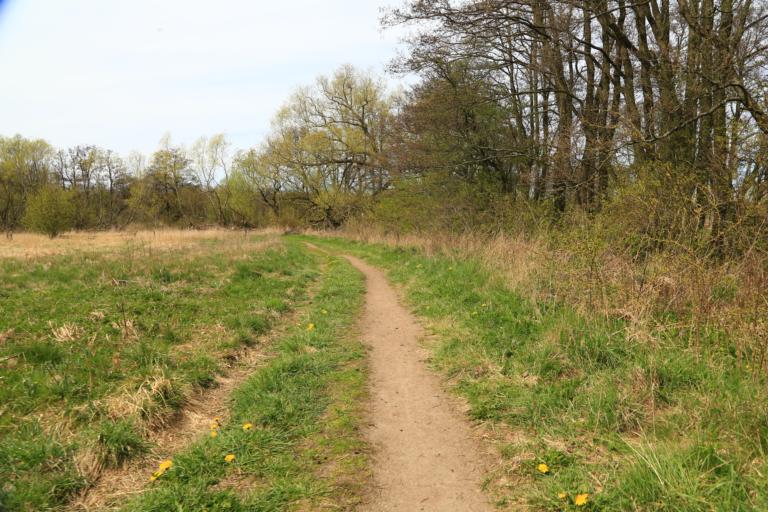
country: SE
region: Halland
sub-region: Varbergs Kommun
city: Varberg
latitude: 57.1299
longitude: 12.2845
